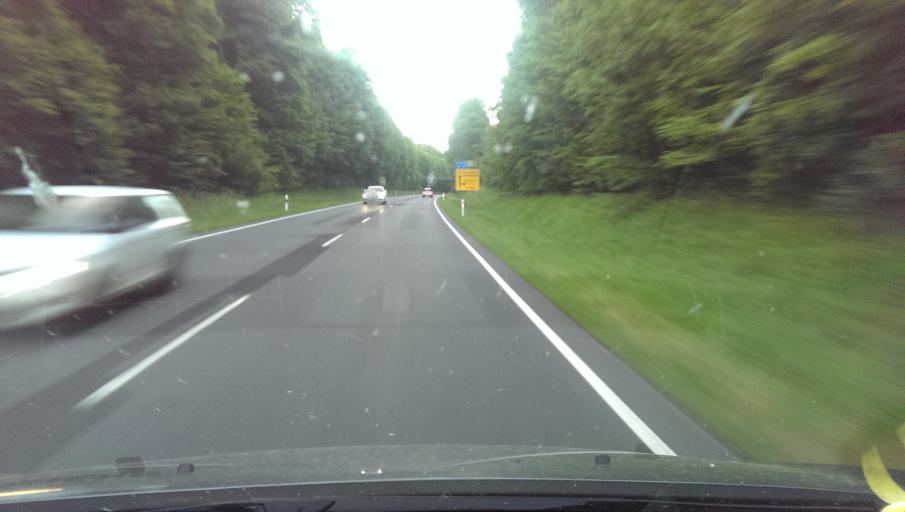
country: DE
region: Bavaria
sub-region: Regierungsbezirk Unterfranken
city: Waldbuttelbrunn
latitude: 49.7866
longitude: 9.8586
